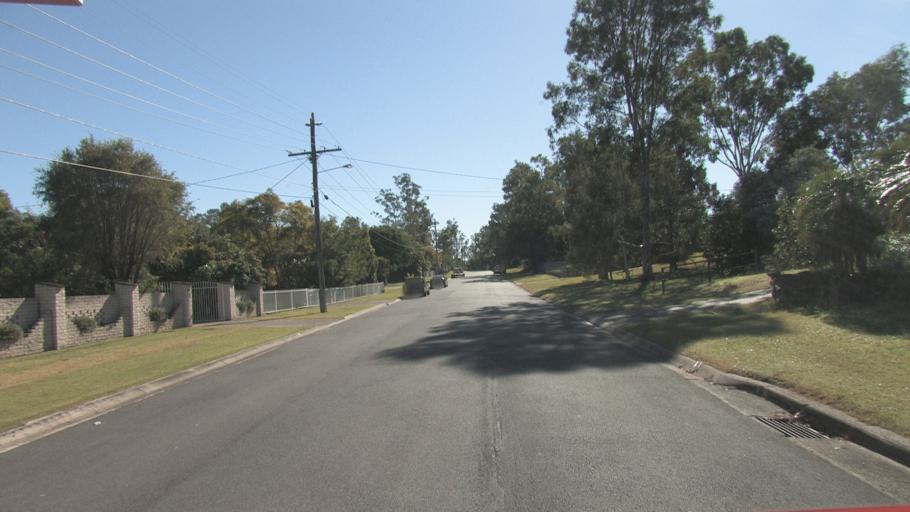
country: AU
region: Queensland
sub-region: Logan
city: Beenleigh
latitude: -27.6982
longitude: 153.2004
